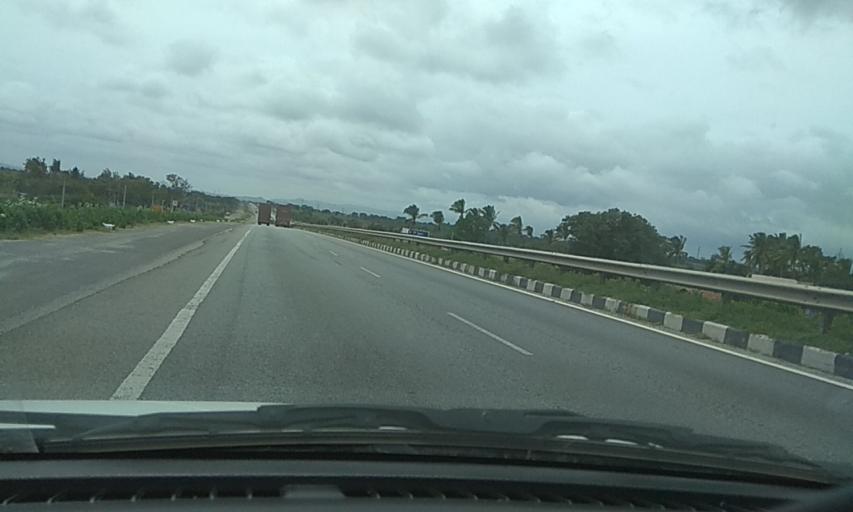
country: IN
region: Karnataka
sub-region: Davanagere
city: Mayakonda
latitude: 14.3093
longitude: 76.2517
